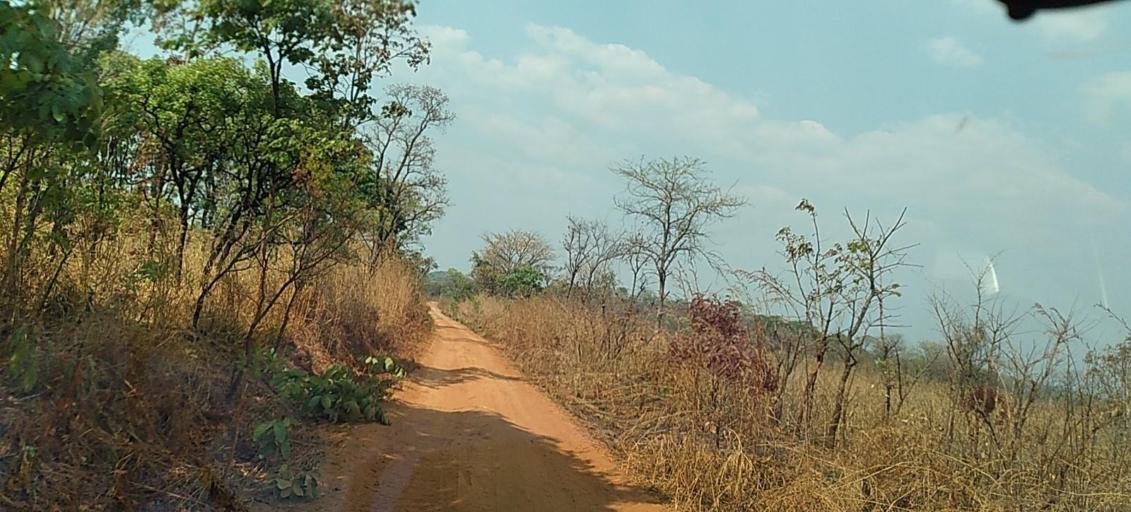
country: ZM
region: North-Western
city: Kasempa
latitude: -13.3087
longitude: 26.0667
